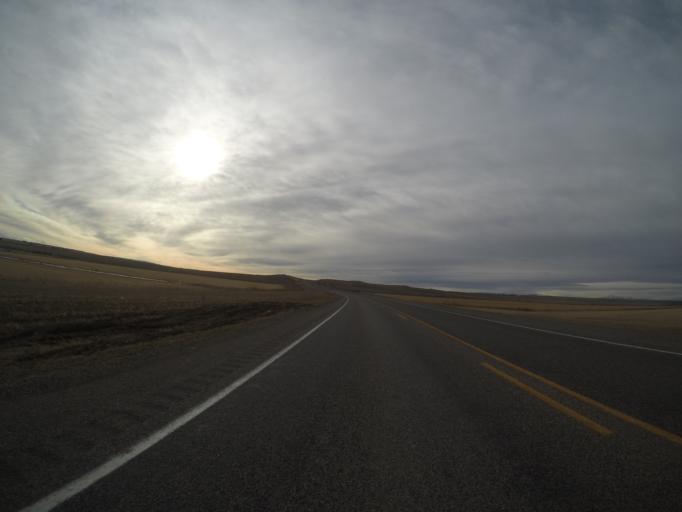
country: US
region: Montana
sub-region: Yellowstone County
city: Laurel
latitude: 45.6110
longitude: -108.8214
